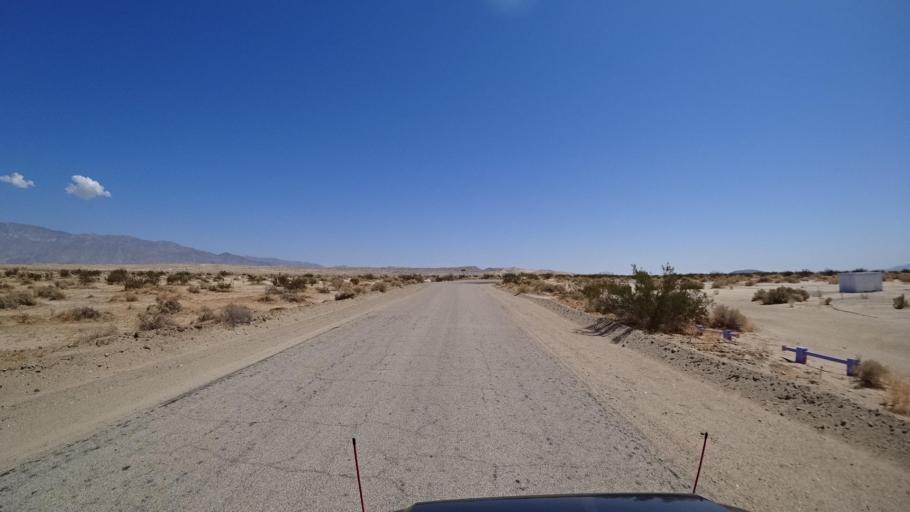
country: US
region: California
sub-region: San Diego County
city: Borrego Springs
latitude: 33.2576
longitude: -116.2965
